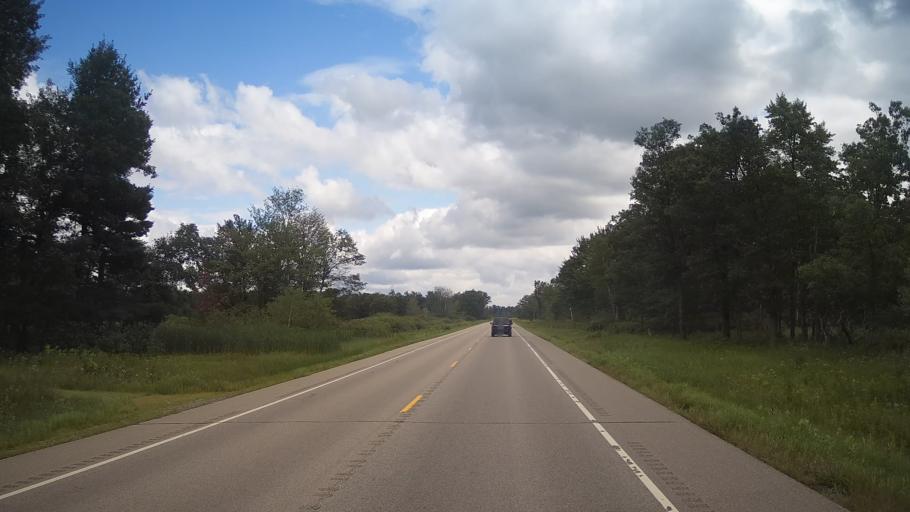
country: US
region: Wisconsin
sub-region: Adams County
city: Friendship
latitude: 44.0257
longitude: -89.6985
